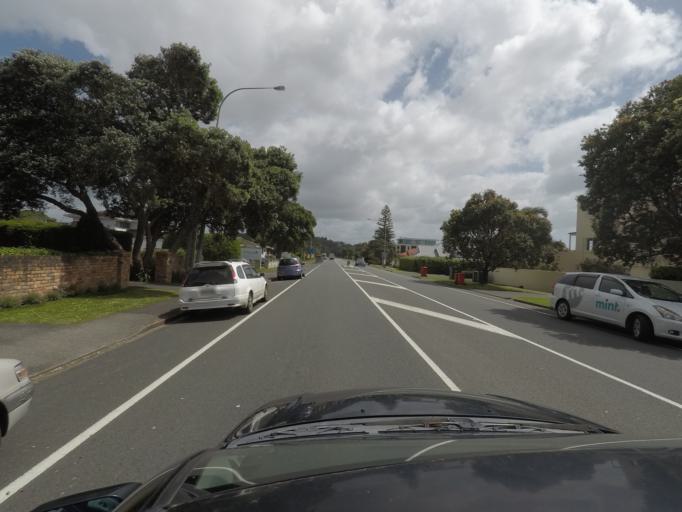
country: NZ
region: Auckland
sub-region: Auckland
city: Rothesay Bay
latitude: -36.5834
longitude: 174.6940
